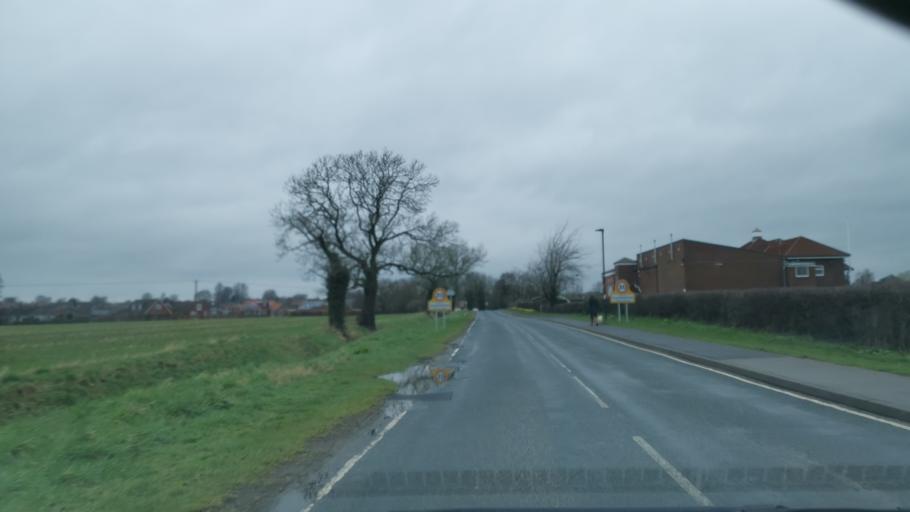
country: GB
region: England
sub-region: City of York
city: Holtby
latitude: 53.9606
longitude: -0.9747
